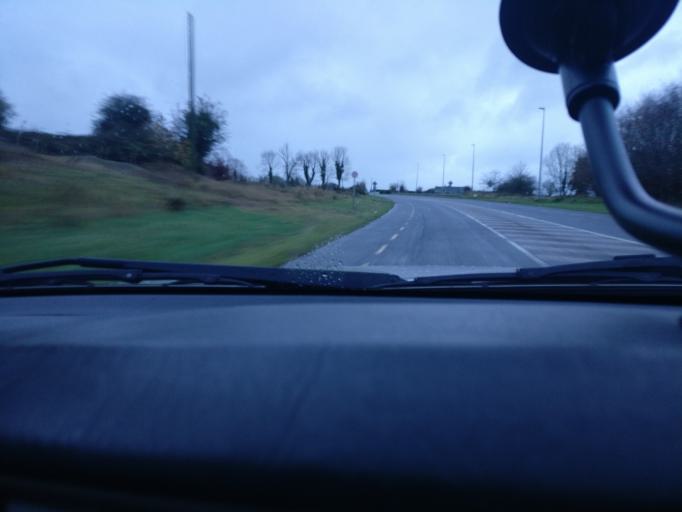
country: IE
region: Connaught
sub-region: County Galway
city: Ballinasloe
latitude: 53.3010
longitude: -8.3203
